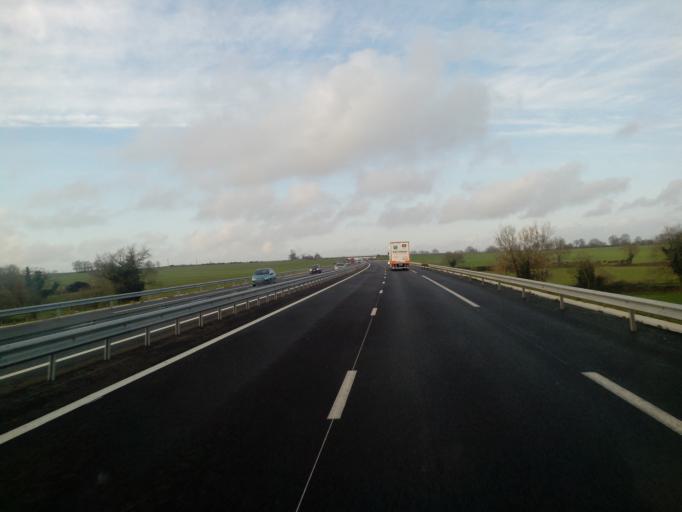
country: FR
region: Poitou-Charentes
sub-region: Departement des Deux-Sevres
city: Nueil-les-Aubiers
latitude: 46.8633
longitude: -0.5705
